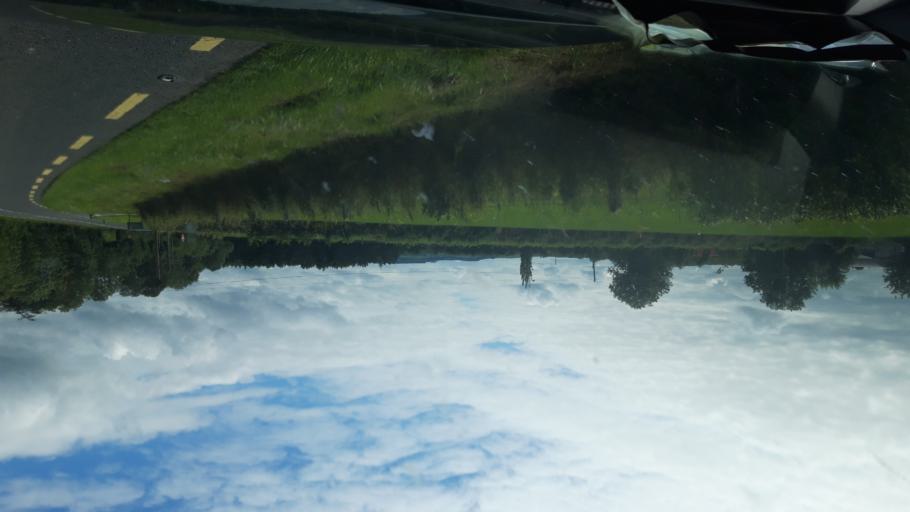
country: IE
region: Leinster
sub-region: Kilkenny
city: Callan
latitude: 52.5238
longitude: -7.4175
